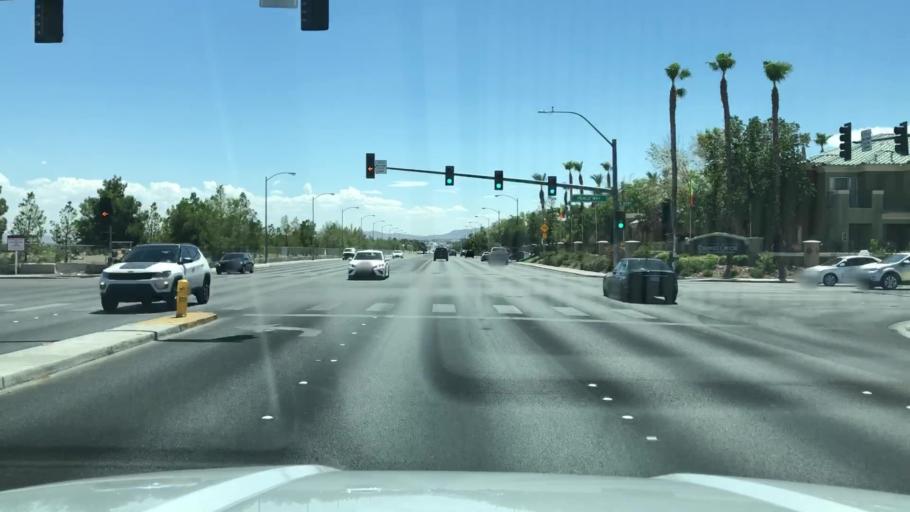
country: US
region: Nevada
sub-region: Clark County
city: Spring Valley
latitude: 36.1077
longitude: -115.2792
